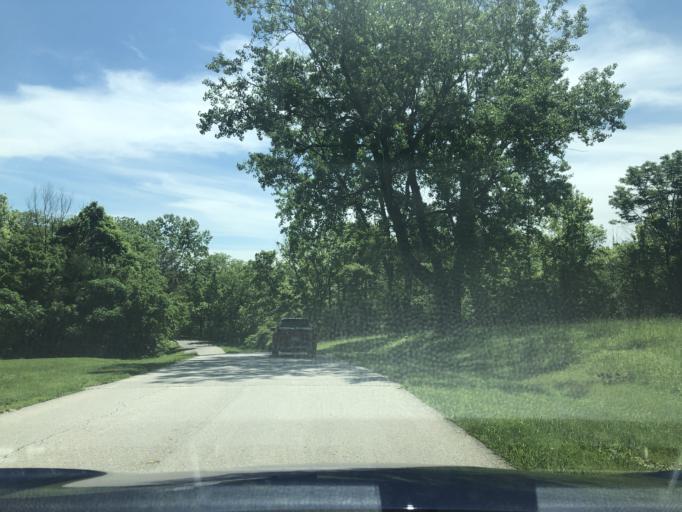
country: US
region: Missouri
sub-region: Platte County
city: Weston
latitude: 39.3905
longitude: -94.8779
